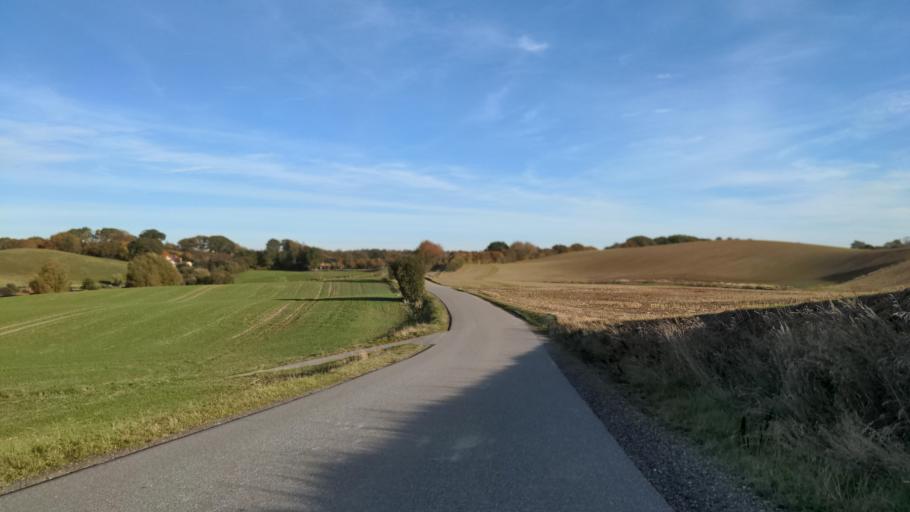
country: DE
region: Schleswig-Holstein
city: Kirchnuchel
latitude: 54.1944
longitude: 10.6902
